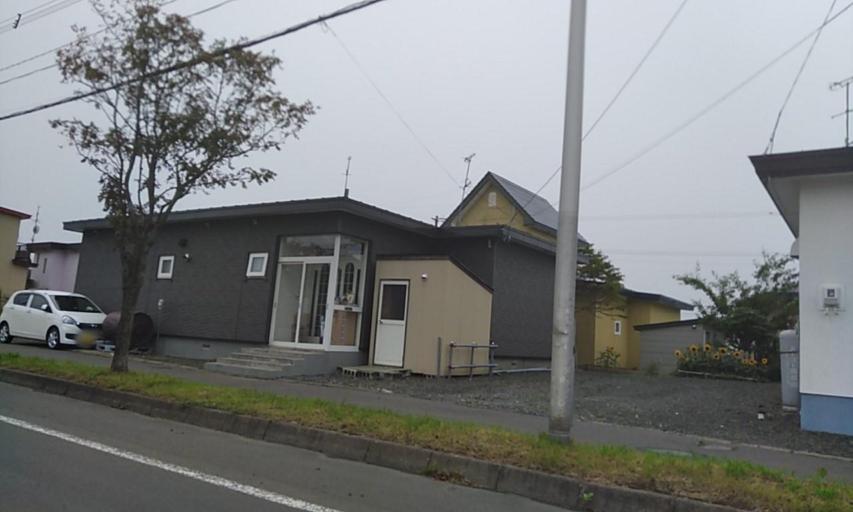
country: JP
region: Hokkaido
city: Nemuro
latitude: 43.3233
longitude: 145.5990
